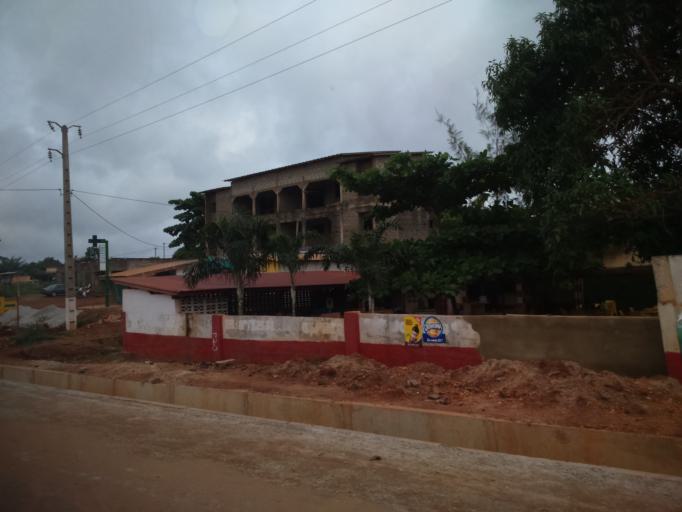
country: CI
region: Moyen-Comoe
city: Abengourou
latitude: 6.7250
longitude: -3.5054
